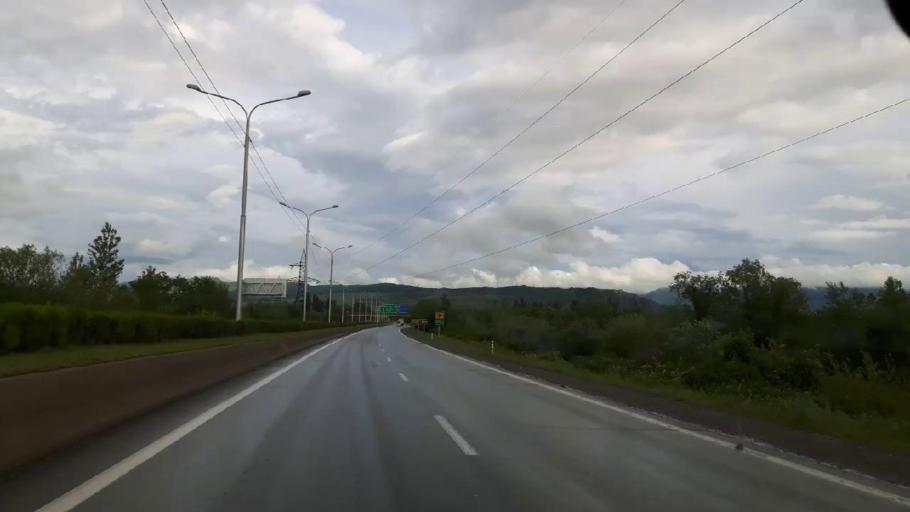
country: GE
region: Shida Kartli
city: Kaspi
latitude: 41.9156
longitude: 44.5556
